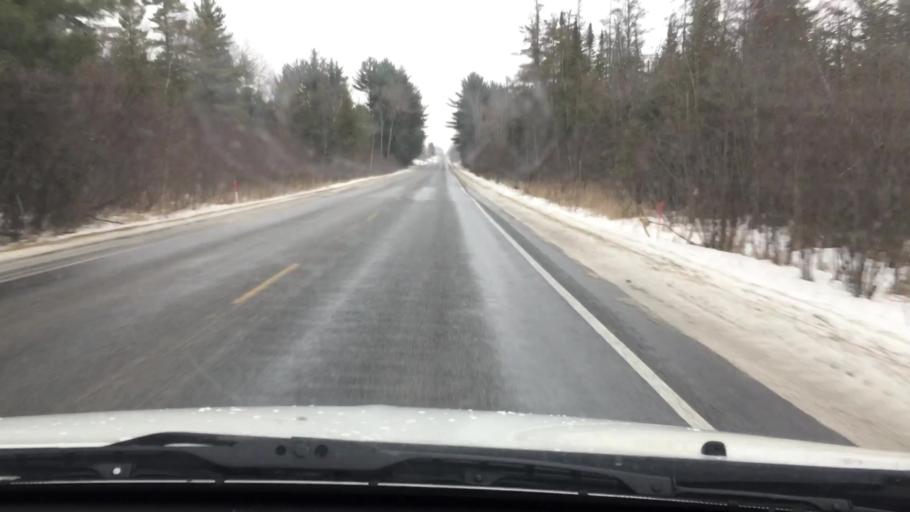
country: US
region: Michigan
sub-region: Osceola County
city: Reed City
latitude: 44.0561
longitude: -85.4439
